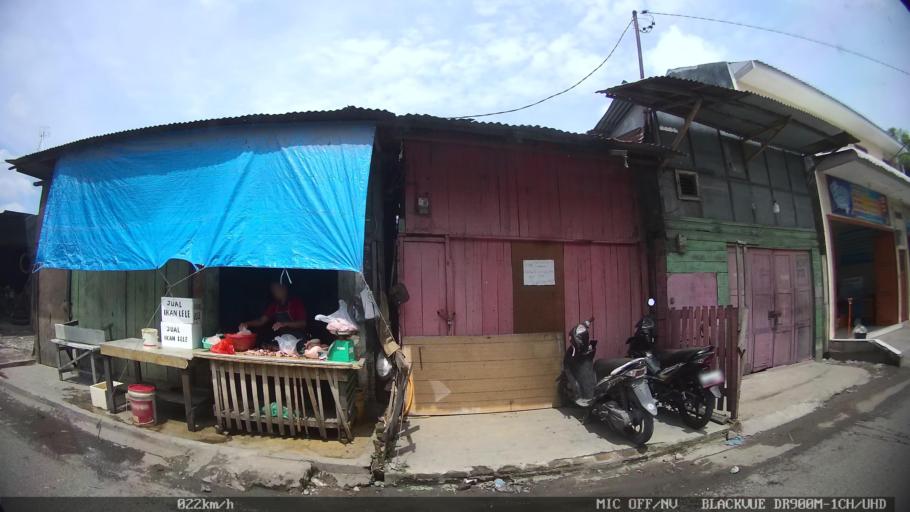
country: ID
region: North Sumatra
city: Medan
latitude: 3.6434
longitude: 98.6873
